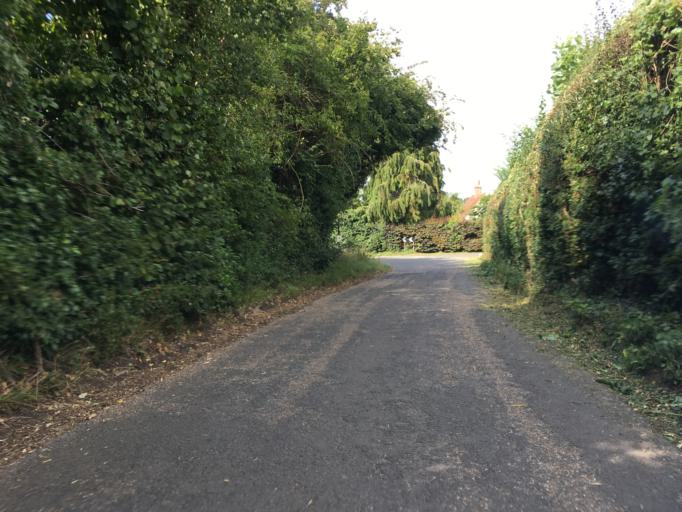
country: GB
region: England
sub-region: Kent
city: Maidstone
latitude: 51.2359
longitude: 0.5225
